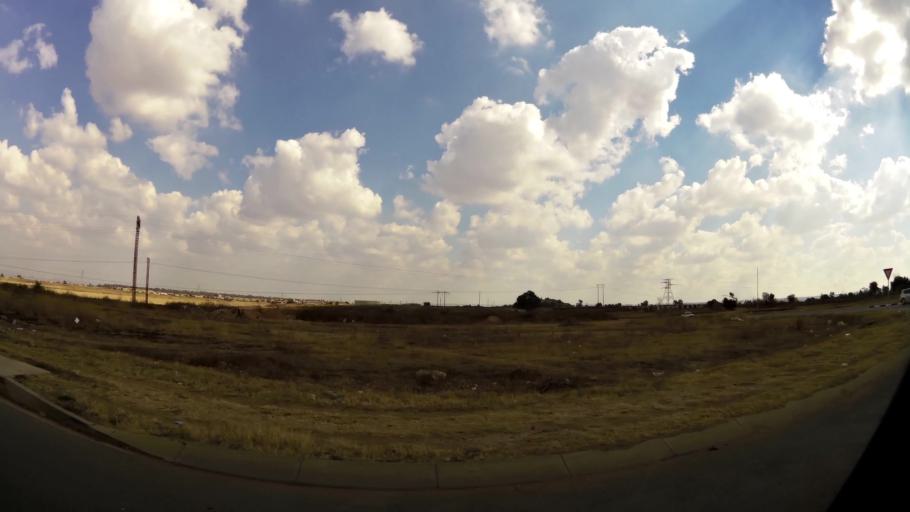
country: ZA
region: Gauteng
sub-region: City of Johannesburg Metropolitan Municipality
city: Roodepoort
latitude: -26.1868
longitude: 27.8560
